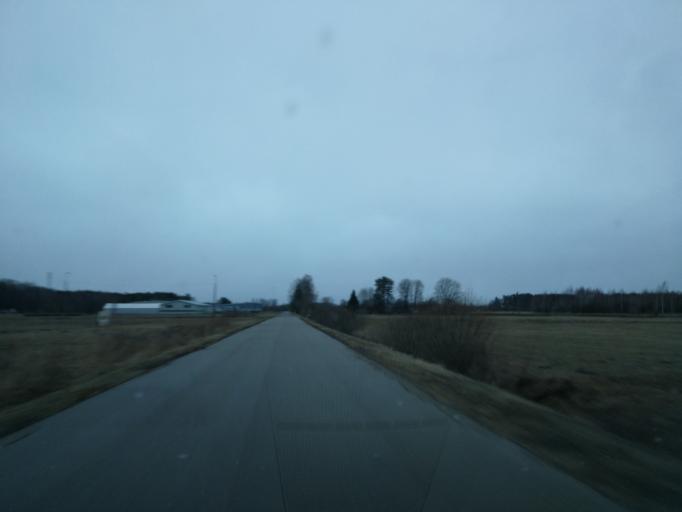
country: LV
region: Adazi
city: Adazi
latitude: 57.0807
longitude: 24.2899
